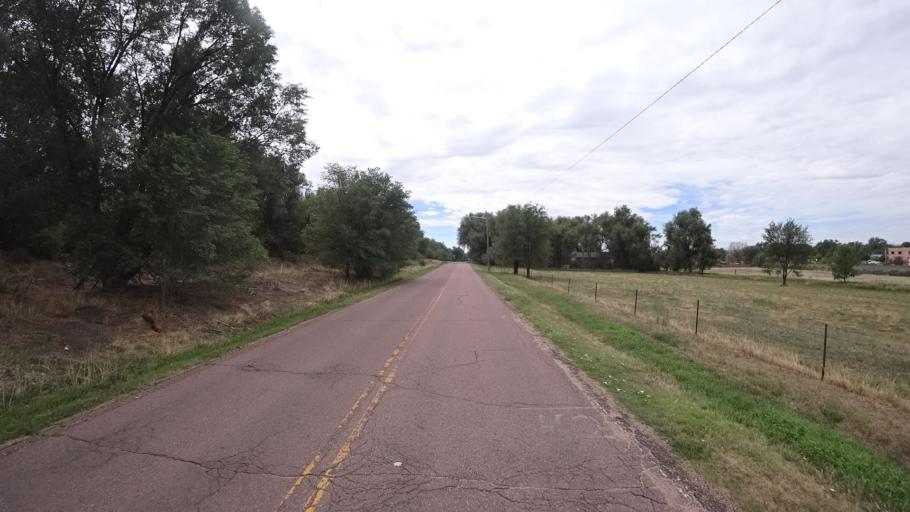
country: US
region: Colorado
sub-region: El Paso County
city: Fountain
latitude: 38.6937
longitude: -104.7032
